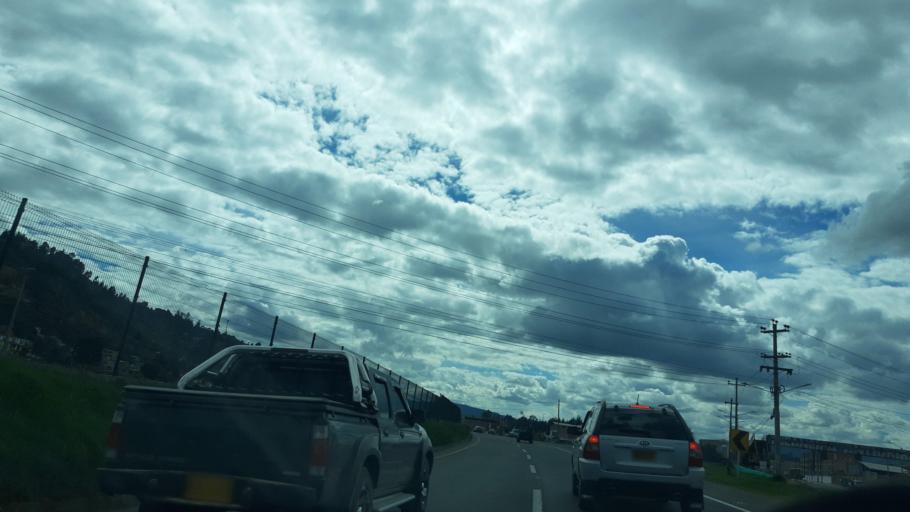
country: CO
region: Cundinamarca
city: Tocancipa
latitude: 4.9681
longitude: -73.9036
